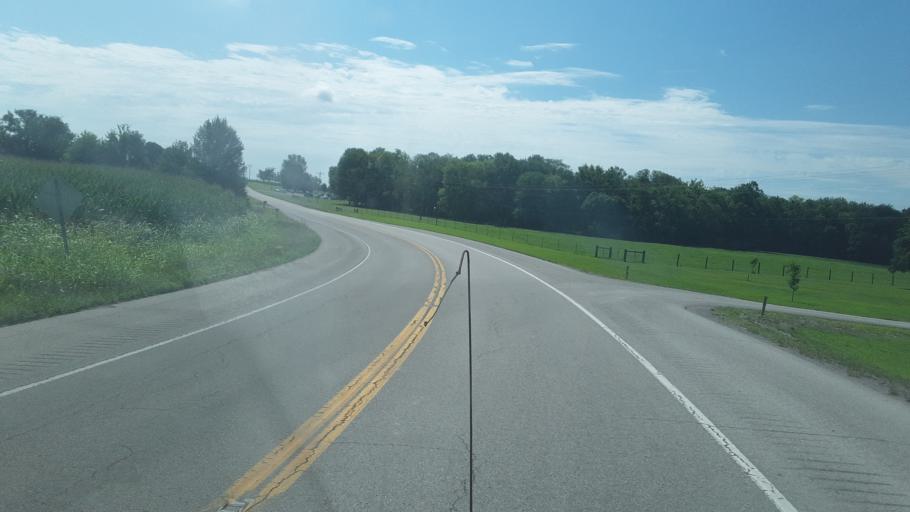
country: US
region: Kentucky
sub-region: Todd County
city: Elkton
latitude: 36.8211
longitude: -87.1992
